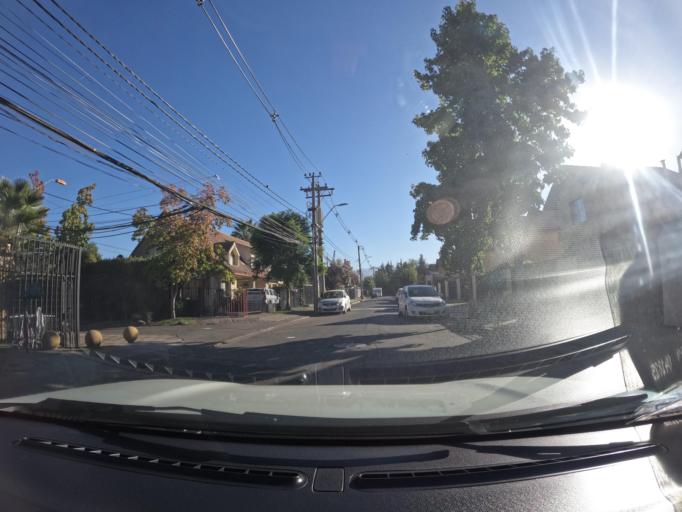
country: CL
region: Santiago Metropolitan
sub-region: Provincia de Santiago
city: Villa Presidente Frei, Nunoa, Santiago, Chile
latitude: -33.4796
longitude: -70.5471
